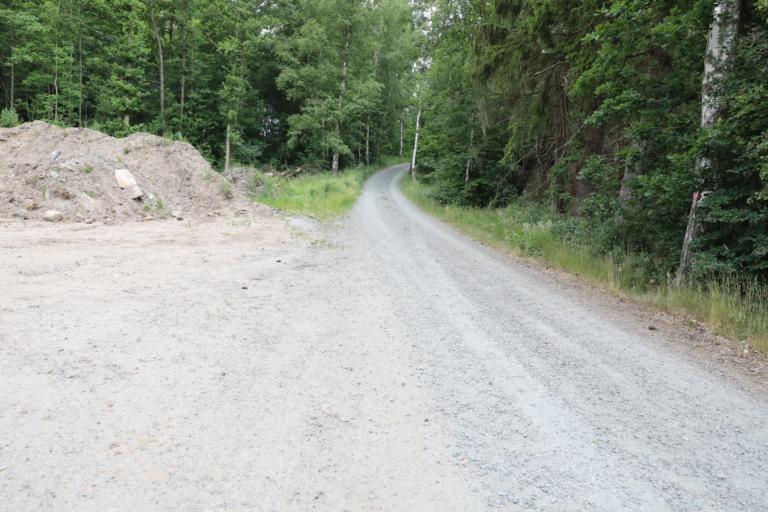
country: SE
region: Halland
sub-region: Varbergs Kommun
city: Varberg
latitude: 57.1635
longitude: 12.2665
